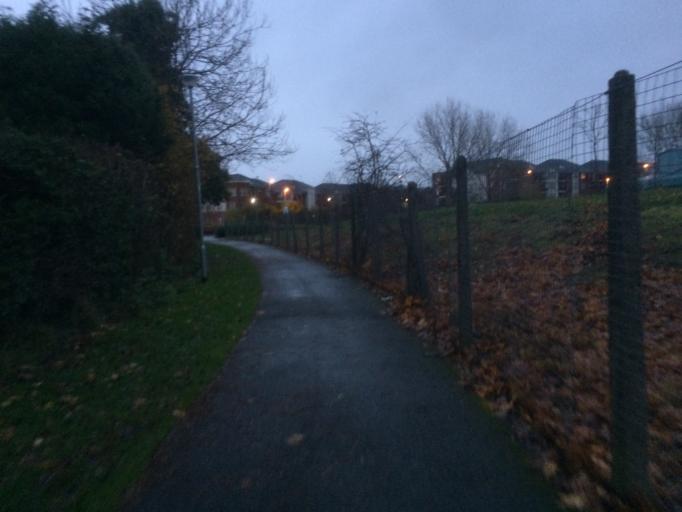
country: GB
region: Scotland
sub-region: East Renfrewshire
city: Giffnock
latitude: 55.8092
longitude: -4.2789
